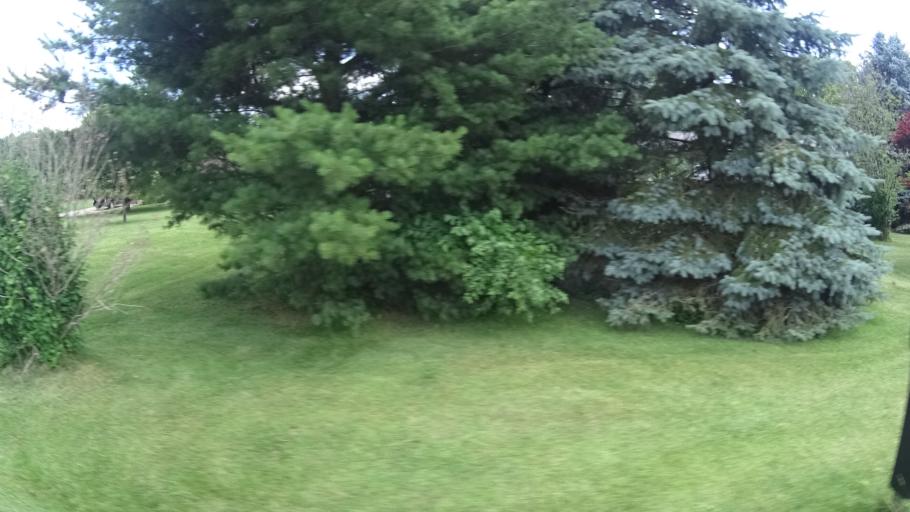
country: US
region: Ohio
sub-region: Erie County
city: Milan
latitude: 41.3030
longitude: -82.5353
